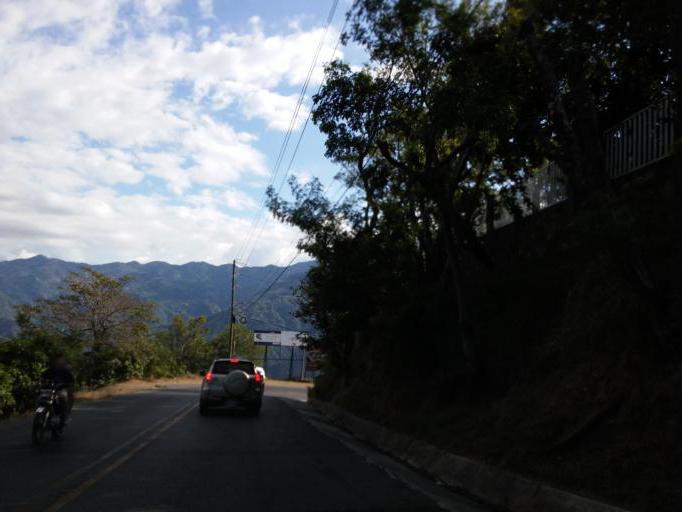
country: CR
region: San Jose
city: San Ignacio
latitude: 9.7972
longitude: -84.1258
